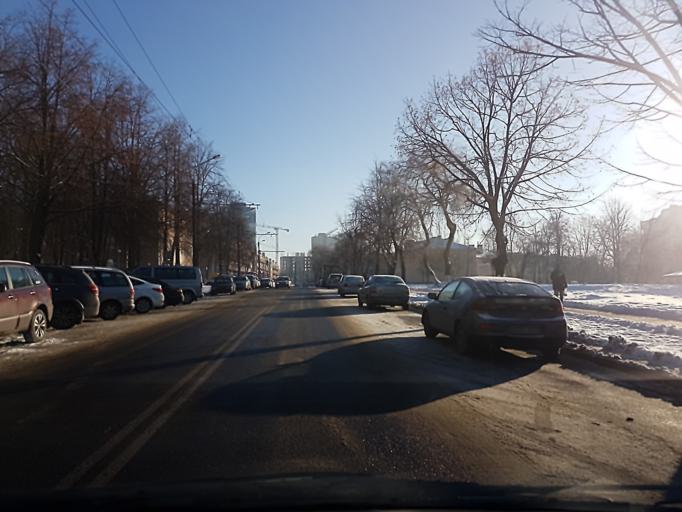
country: BY
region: Minsk
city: Minsk
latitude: 53.8917
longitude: 27.5141
